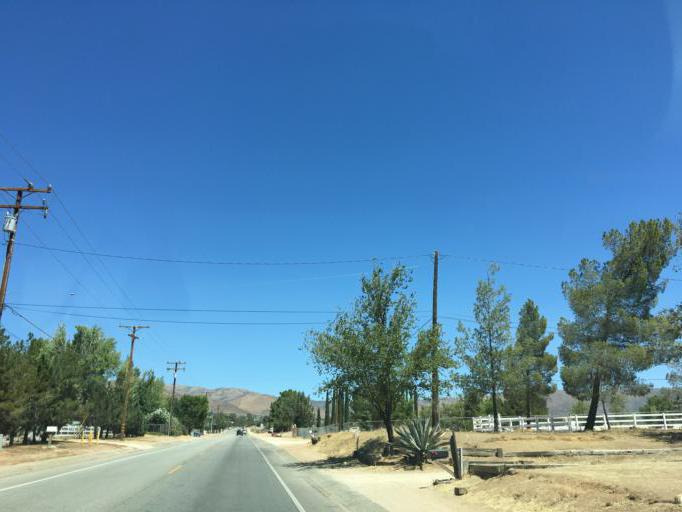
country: US
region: California
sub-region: Los Angeles County
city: Acton
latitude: 34.4746
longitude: -118.1974
